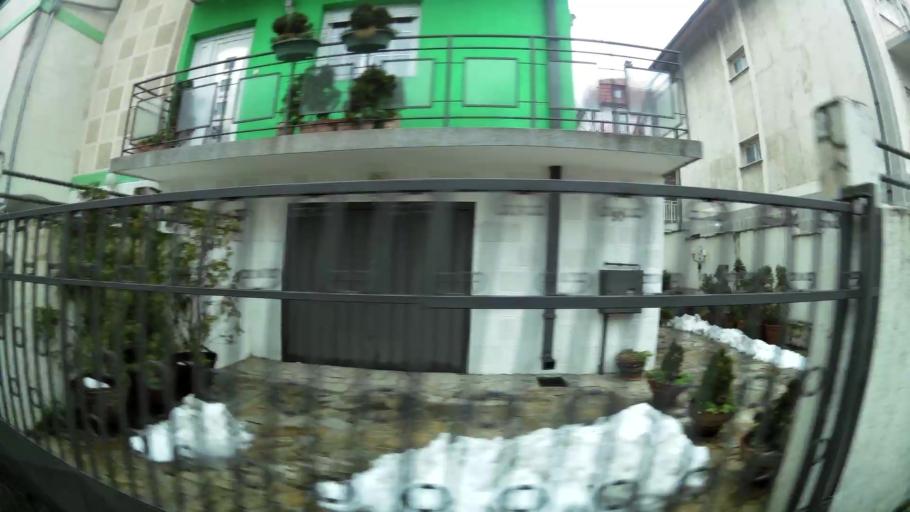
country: RS
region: Central Serbia
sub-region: Belgrade
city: Vozdovac
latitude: 44.7733
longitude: 20.4807
